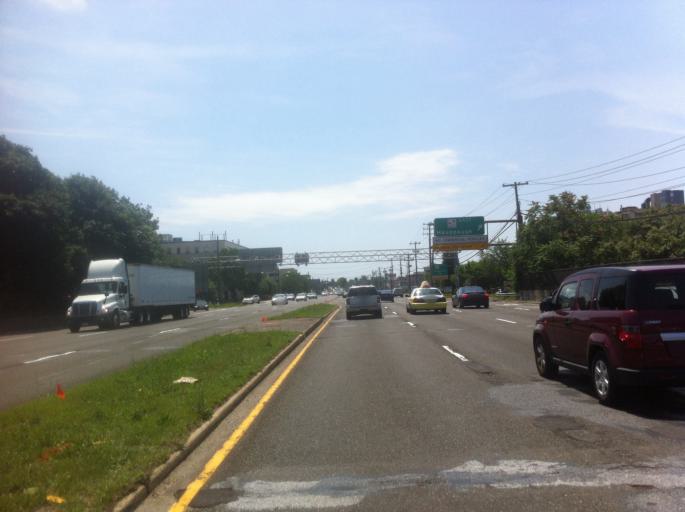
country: US
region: New York
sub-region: Nassau County
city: Jericho
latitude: 40.7836
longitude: -73.5328
